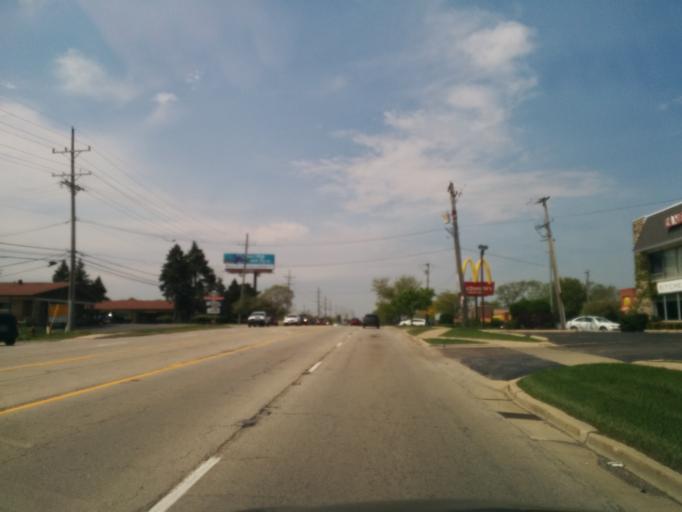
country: US
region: Illinois
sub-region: DuPage County
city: Lombard
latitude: 41.8604
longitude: -88.0087
